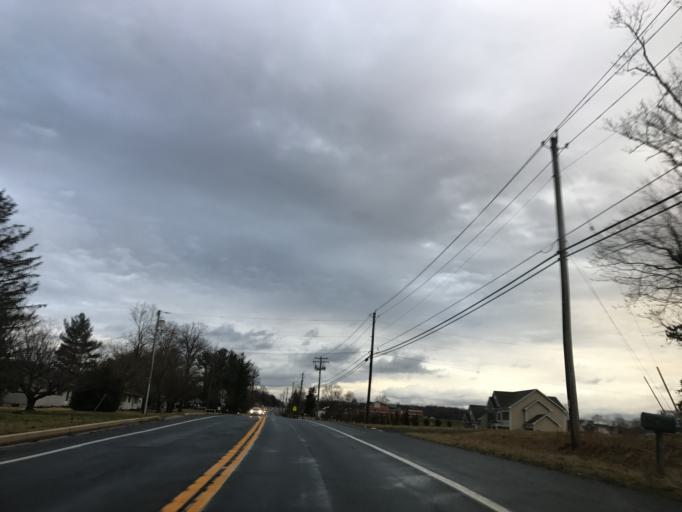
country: US
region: Maryland
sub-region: Harford County
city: Riverside
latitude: 39.4956
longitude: -76.2615
